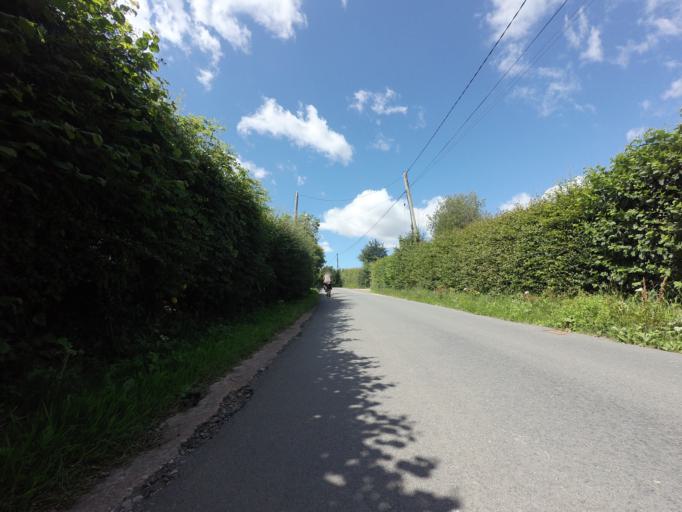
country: GB
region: England
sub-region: East Sussex
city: Horam
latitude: 50.9113
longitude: 0.2121
